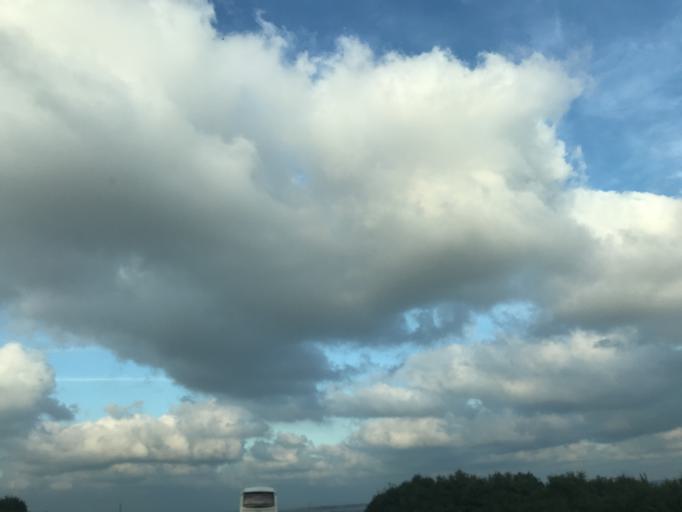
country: TR
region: Istanbul
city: Durusu
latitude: 41.2619
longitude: 28.6917
